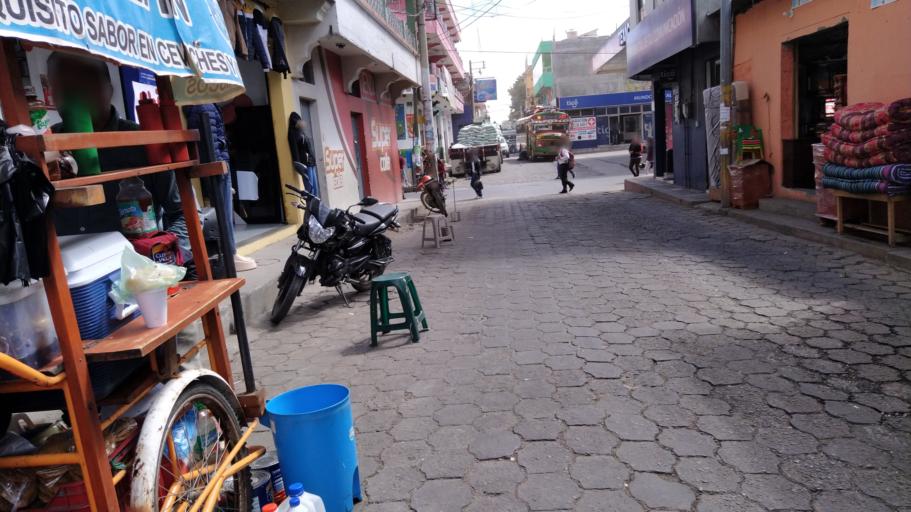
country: GT
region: Quetzaltenango
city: Ostuncalco
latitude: 14.8701
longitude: -91.6222
